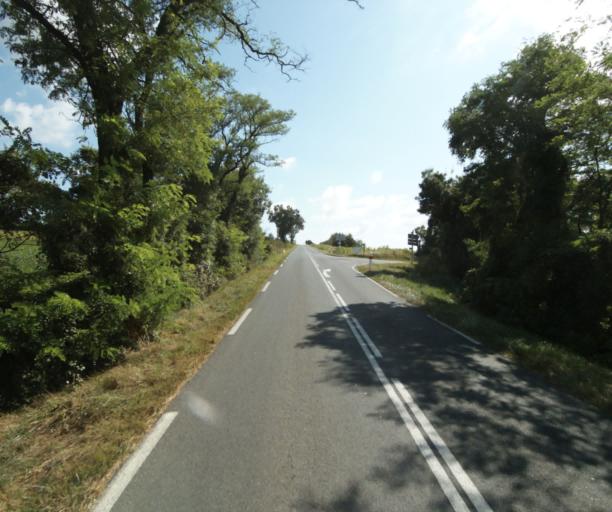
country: FR
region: Midi-Pyrenees
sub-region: Departement de la Haute-Garonne
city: Avignonet-Lauragais
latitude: 43.4453
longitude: 1.8089
